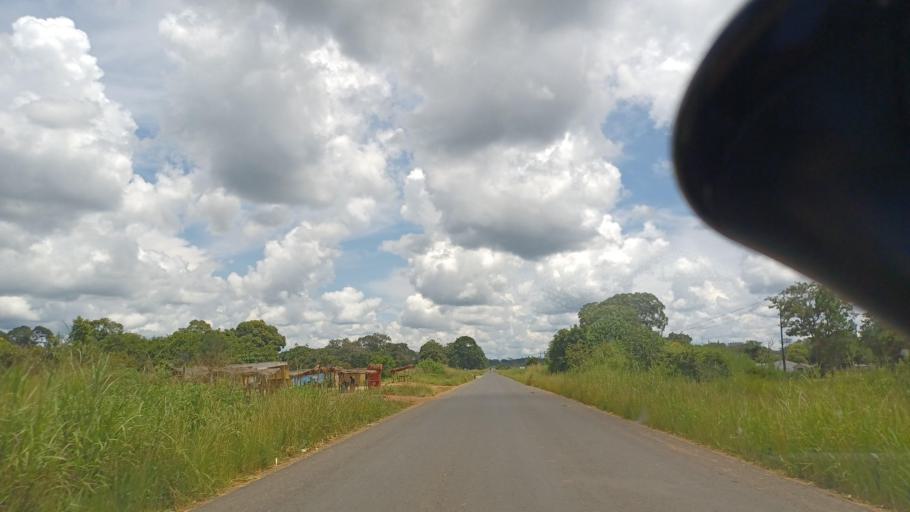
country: ZM
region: North-Western
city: Solwezi
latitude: -12.4235
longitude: 26.2210
